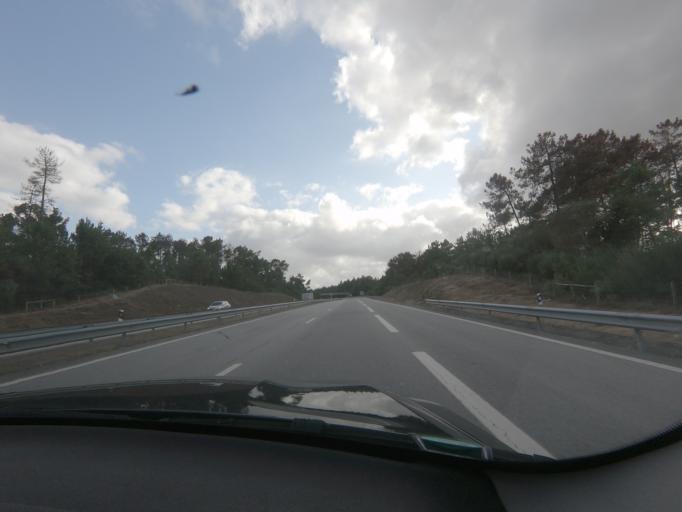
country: PT
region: Viseu
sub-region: Viseu
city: Abraveses
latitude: 40.6968
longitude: -7.9598
